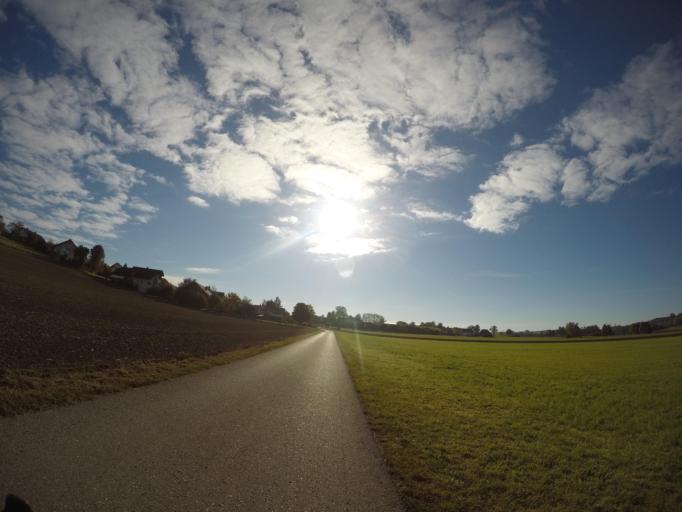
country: DE
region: Baden-Wuerttemberg
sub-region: Tuebingen Region
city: Herbertingen
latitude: 48.0504
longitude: 9.4468
